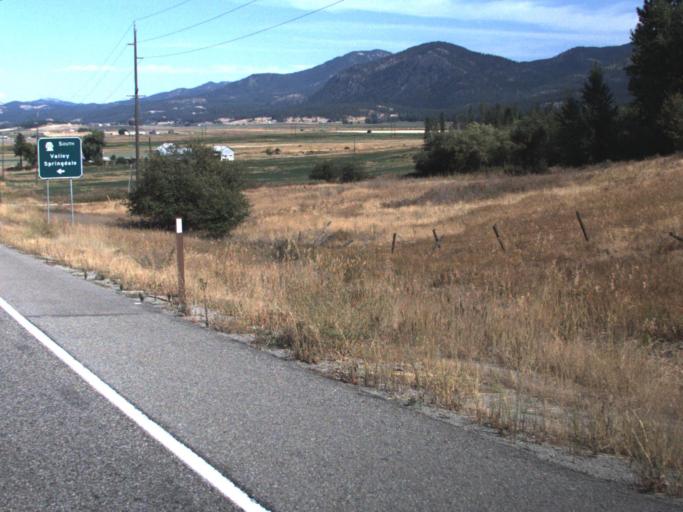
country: US
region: Washington
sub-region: Stevens County
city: Chewelah
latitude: 48.2070
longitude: -117.7152
